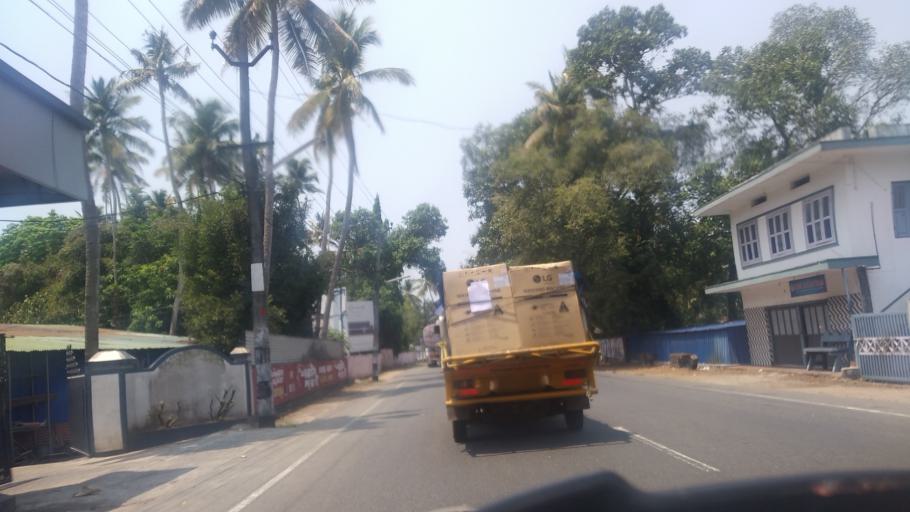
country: IN
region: Kerala
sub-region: Thrissur District
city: Kodungallur
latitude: 10.2698
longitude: 76.1777
